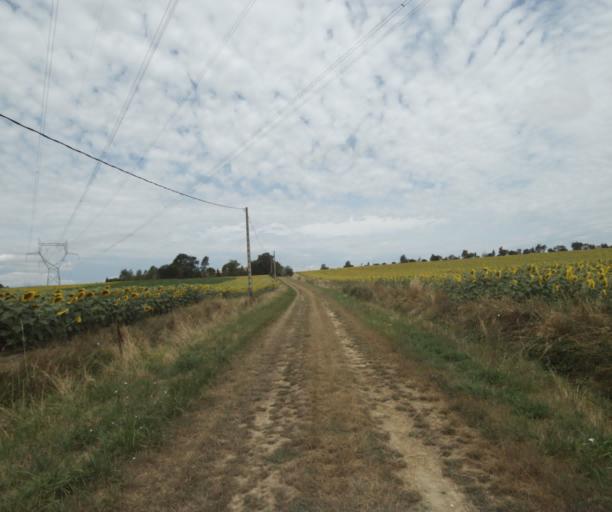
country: FR
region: Midi-Pyrenees
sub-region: Departement de la Haute-Garonne
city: Saint-Felix-Lauragais
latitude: 43.4143
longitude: 1.9075
